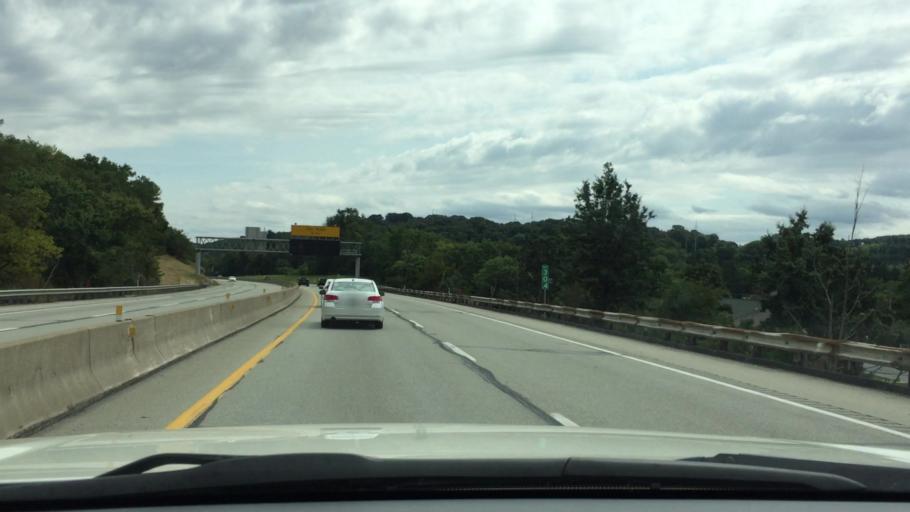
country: US
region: Pennsylvania
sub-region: Allegheny County
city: Bradford Woods
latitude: 40.6576
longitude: -80.0836
